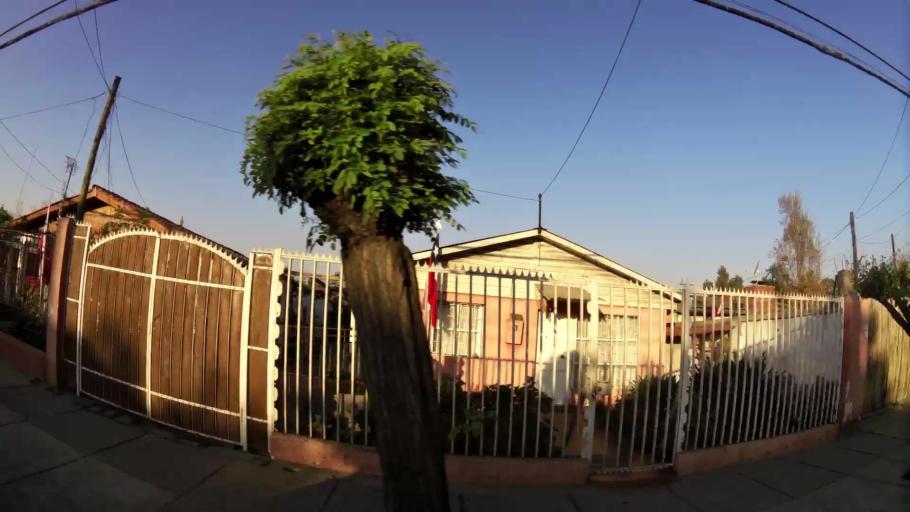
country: CL
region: Santiago Metropolitan
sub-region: Provincia de Santiago
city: La Pintana
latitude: -33.5260
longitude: -70.6247
